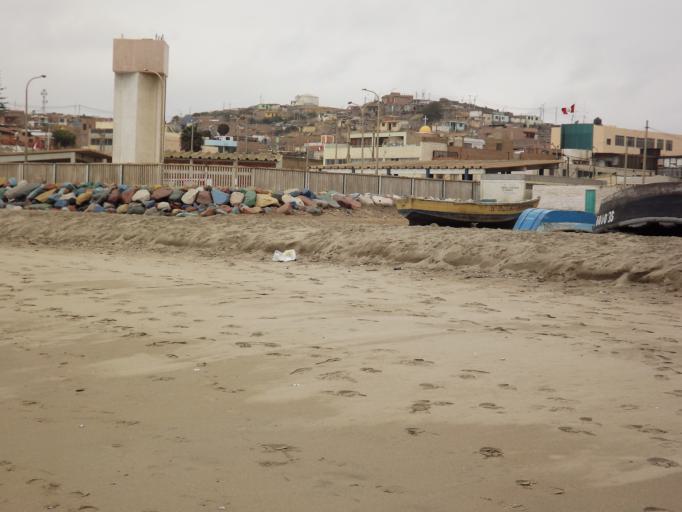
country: PE
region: Lima
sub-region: Barranca
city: Puerto Supe
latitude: -10.8010
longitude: -77.7468
